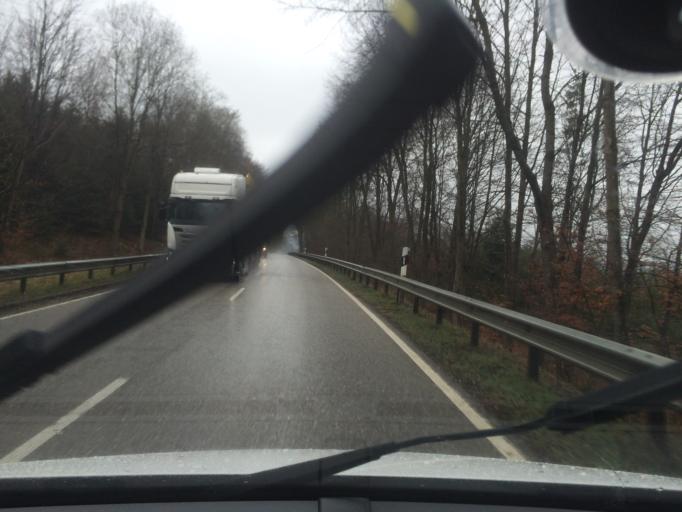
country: DE
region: Bavaria
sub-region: Upper Bavaria
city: Bruck
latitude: 47.9810
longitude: 11.9472
